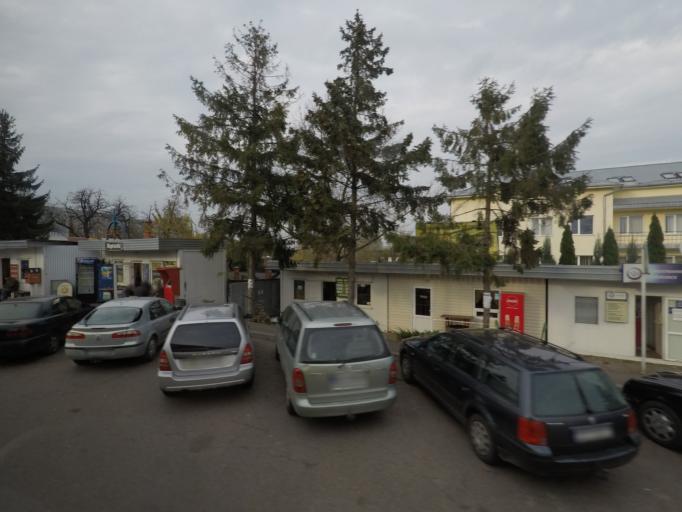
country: PL
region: Subcarpathian Voivodeship
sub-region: Powiat przemyski
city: Medyka
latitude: 49.7996
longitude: 22.9548
